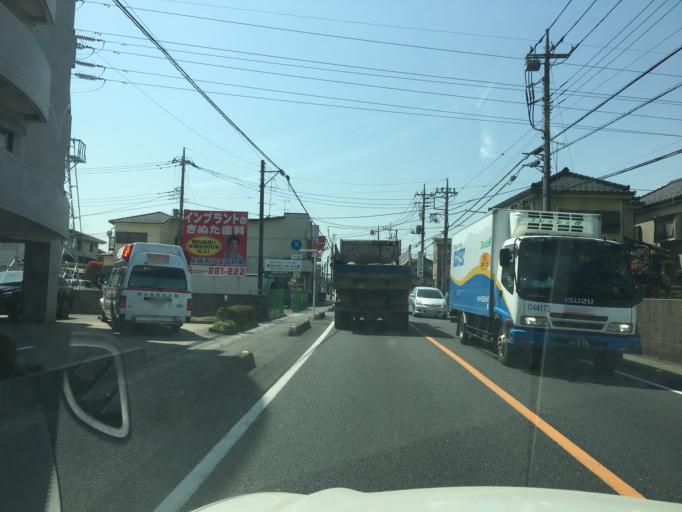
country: JP
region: Saitama
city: Sayama
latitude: 35.8267
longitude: 139.4139
